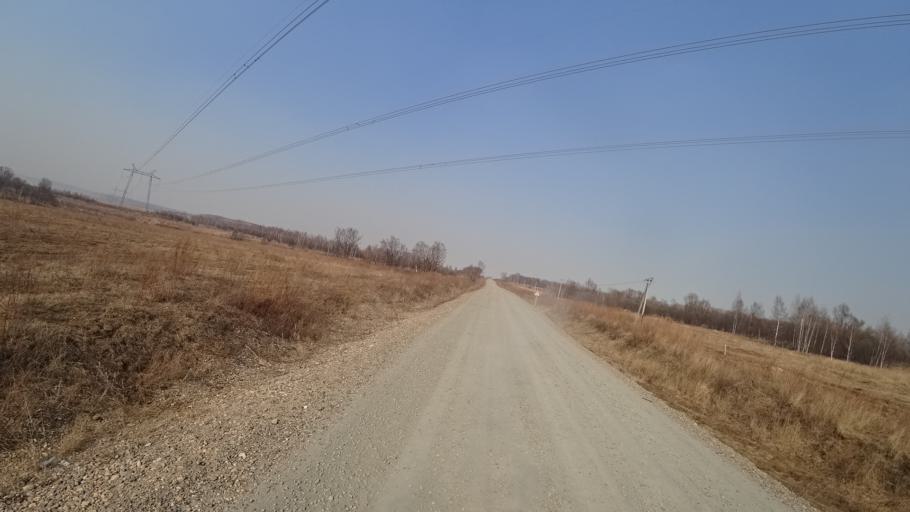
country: RU
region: Amur
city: Novobureyskiy
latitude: 49.8150
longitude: 129.9747
